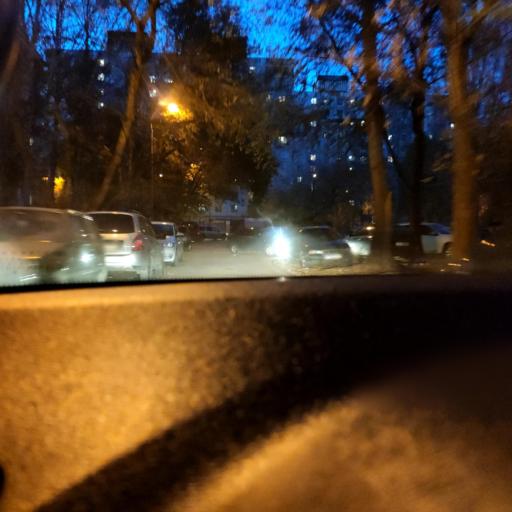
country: RU
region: Samara
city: Samara
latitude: 53.2476
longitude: 50.2503
